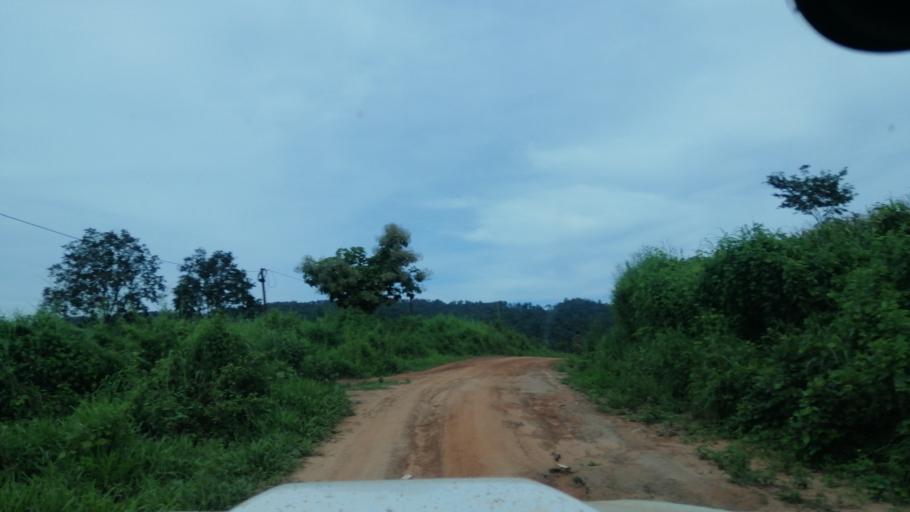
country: TH
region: Loei
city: Na Haeo
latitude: 17.5829
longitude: 101.1411
